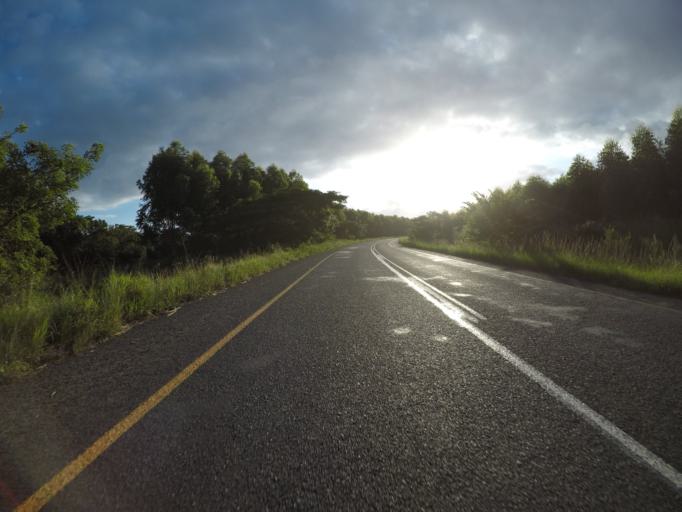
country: ZA
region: KwaZulu-Natal
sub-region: uMkhanyakude District Municipality
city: Mtubatuba
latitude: -28.4120
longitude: 32.1939
